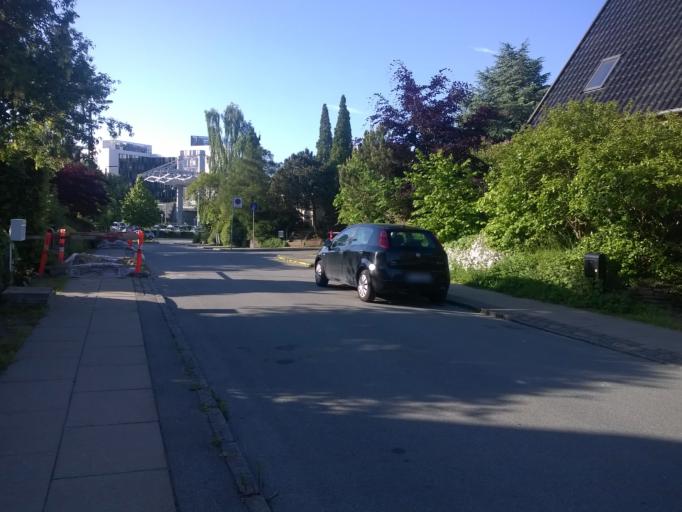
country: DK
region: Capital Region
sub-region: Kobenhavn
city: Vanlose
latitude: 55.6873
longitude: 12.4985
